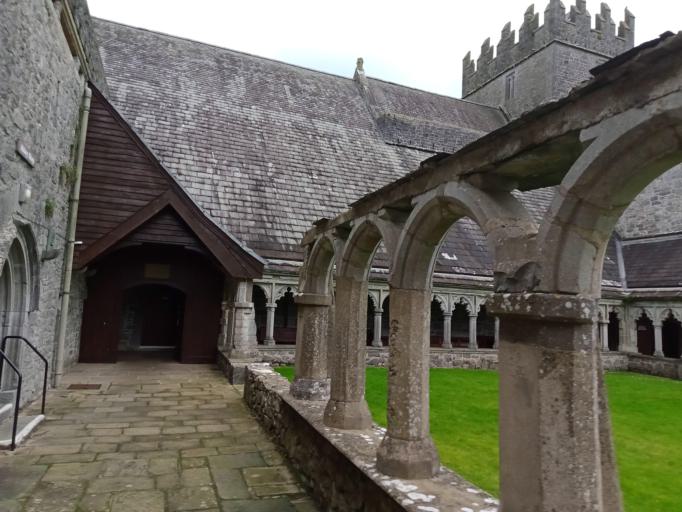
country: IE
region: Munster
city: Thurles
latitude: 52.6393
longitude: -7.8682
